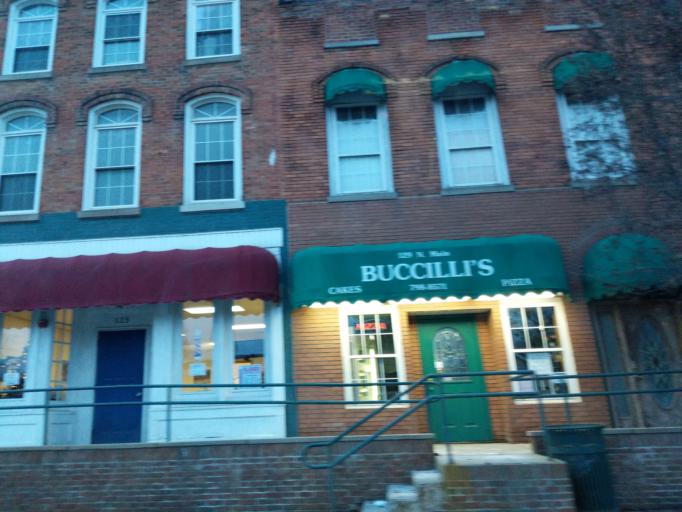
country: US
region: Michigan
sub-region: Lapeer County
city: Almont
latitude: 42.9210
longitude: -83.0453
